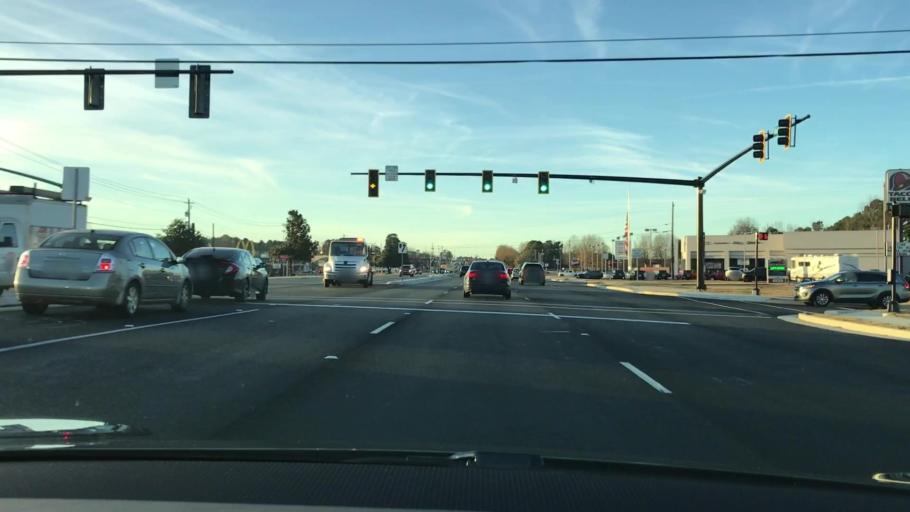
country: US
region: Georgia
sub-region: Gwinnett County
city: Sugar Hill
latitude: 34.0939
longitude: -84.0095
